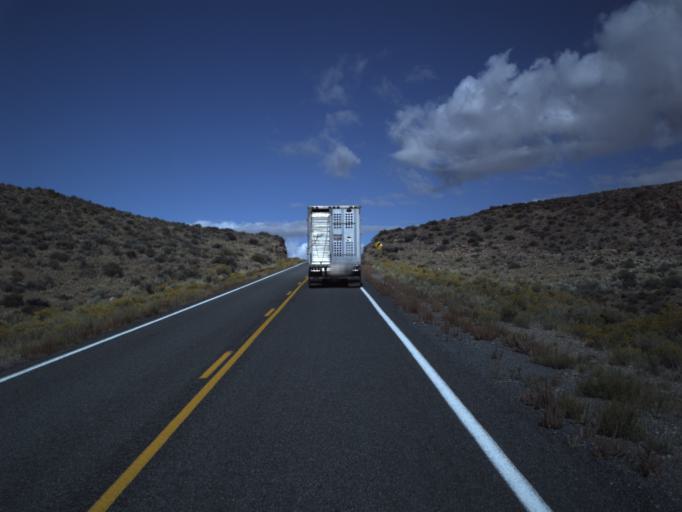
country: US
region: Utah
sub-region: Beaver County
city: Milford
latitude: 38.6150
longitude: -113.8414
